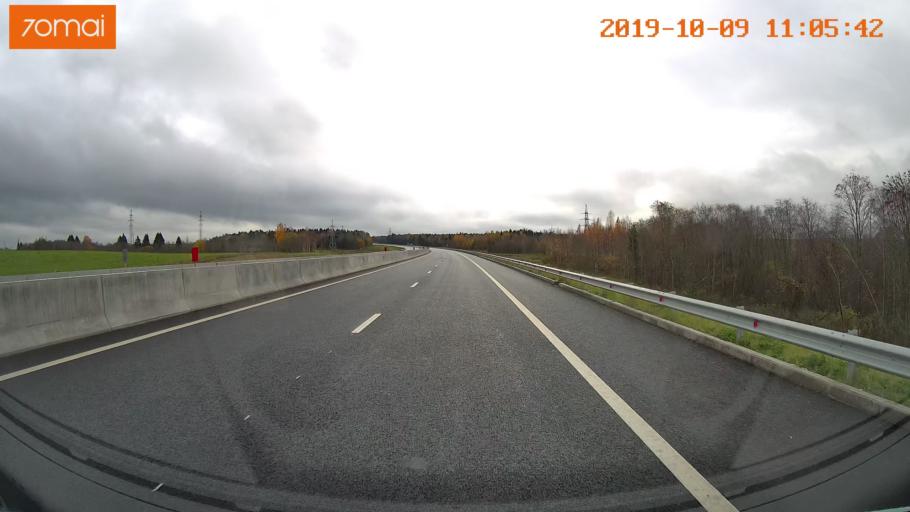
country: RU
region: Vologda
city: Molochnoye
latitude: 59.1963
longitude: 39.7580
